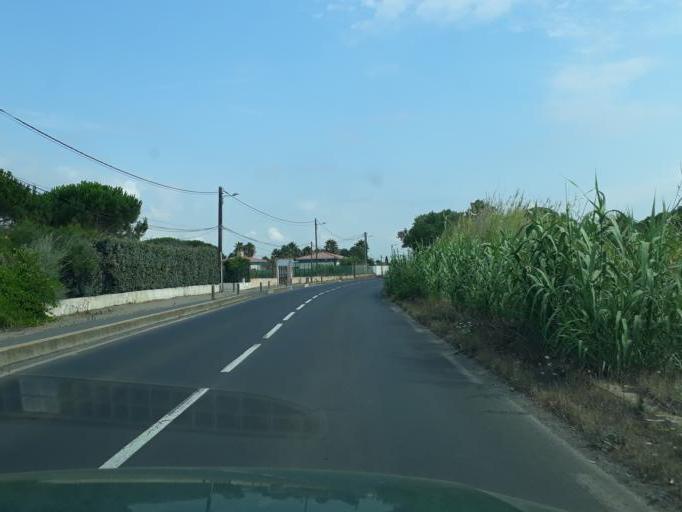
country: FR
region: Languedoc-Roussillon
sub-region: Departement de l'Herault
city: Agde
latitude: 43.2824
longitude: 3.4818
